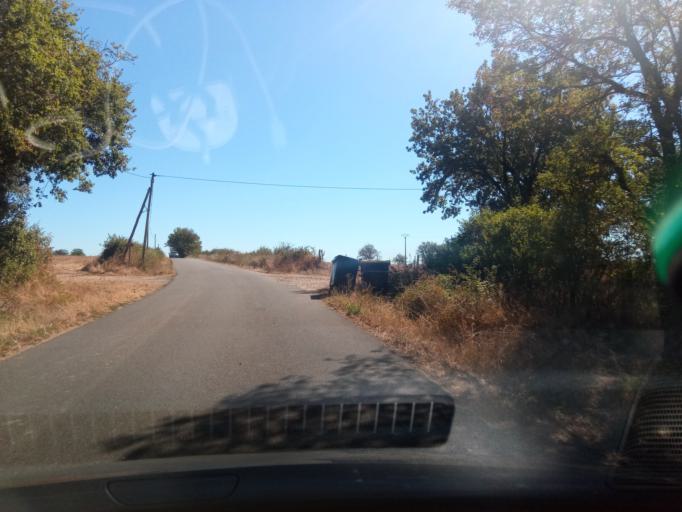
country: FR
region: Poitou-Charentes
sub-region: Departement de la Vienne
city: Saulge
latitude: 46.3791
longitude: 0.8957
